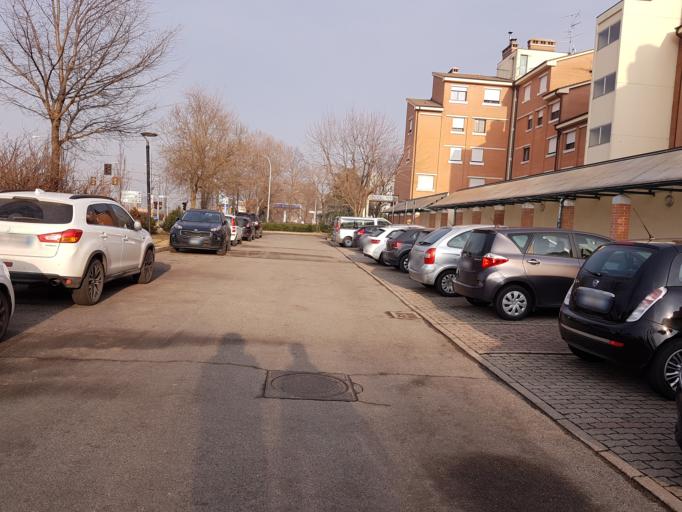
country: IT
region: Emilia-Romagna
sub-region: Provincia di Bologna
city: Quarto Inferiore
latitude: 44.5120
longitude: 11.3858
